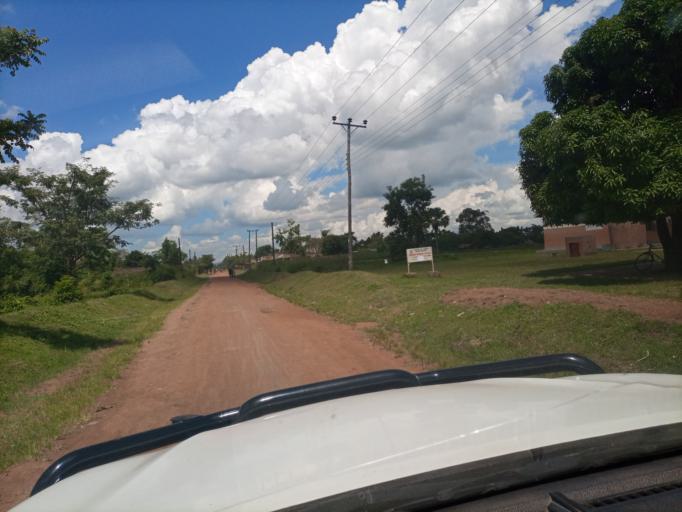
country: UG
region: Eastern Region
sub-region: Tororo District
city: Tororo
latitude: 0.6713
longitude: 34.0041
